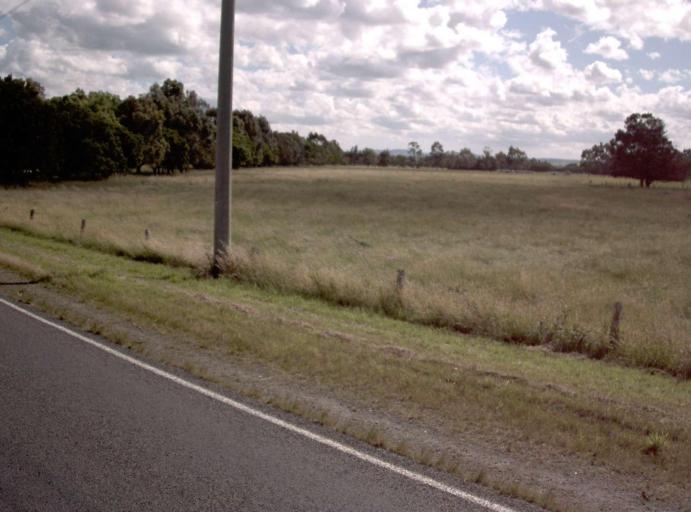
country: AU
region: Victoria
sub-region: Latrobe
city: Morwell
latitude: -38.2885
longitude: 146.4300
